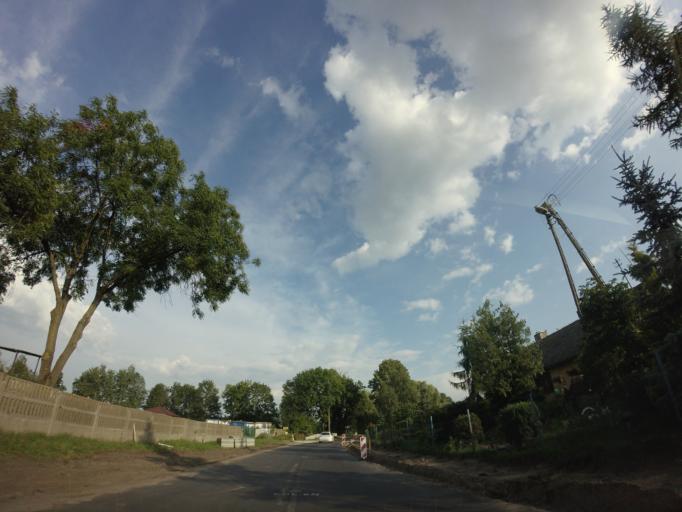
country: PL
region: Lublin Voivodeship
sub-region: Powiat lubartowski
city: Przytoczno
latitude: 51.6120
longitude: 22.2772
